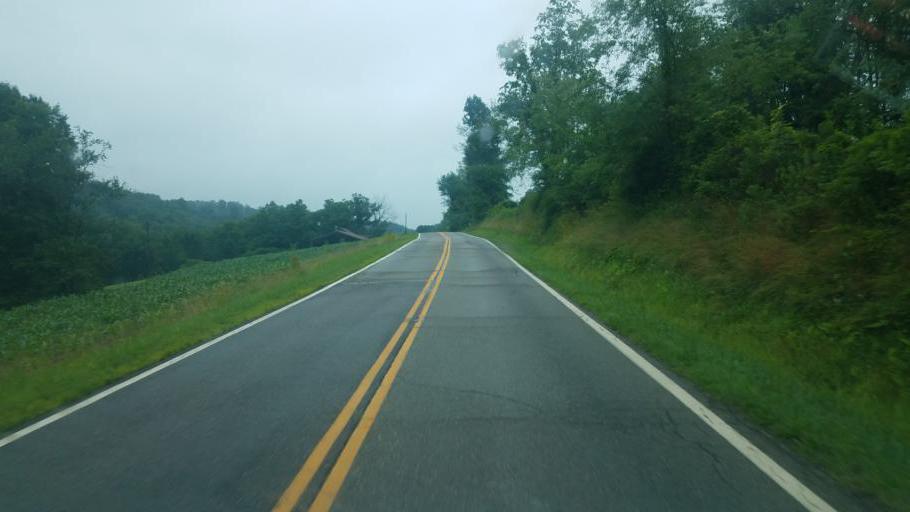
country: US
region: Ohio
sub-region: Carroll County
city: Carrollton
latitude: 40.4637
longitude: -80.9812
